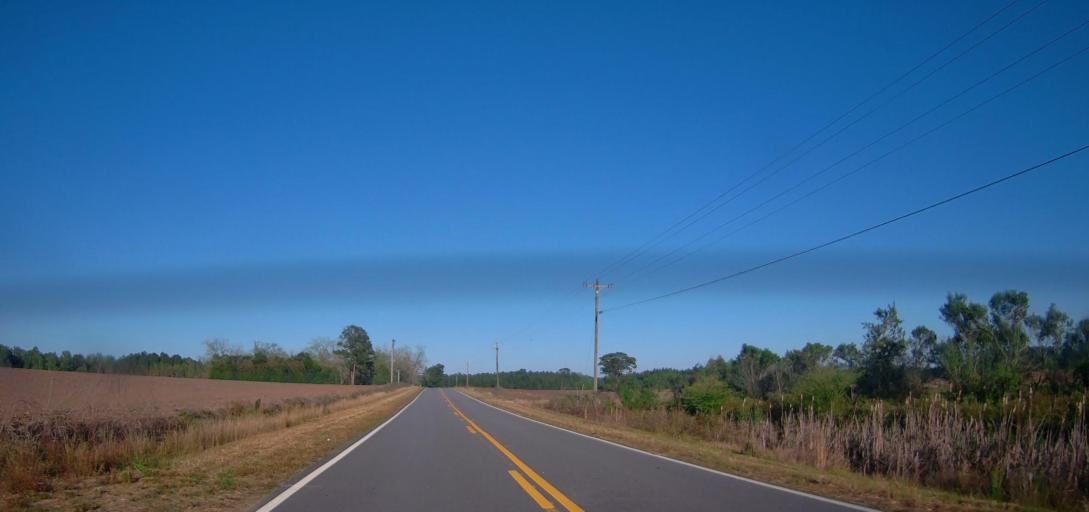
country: US
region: Georgia
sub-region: Ben Hill County
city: Fitzgerald
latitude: 31.6563
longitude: -83.1672
